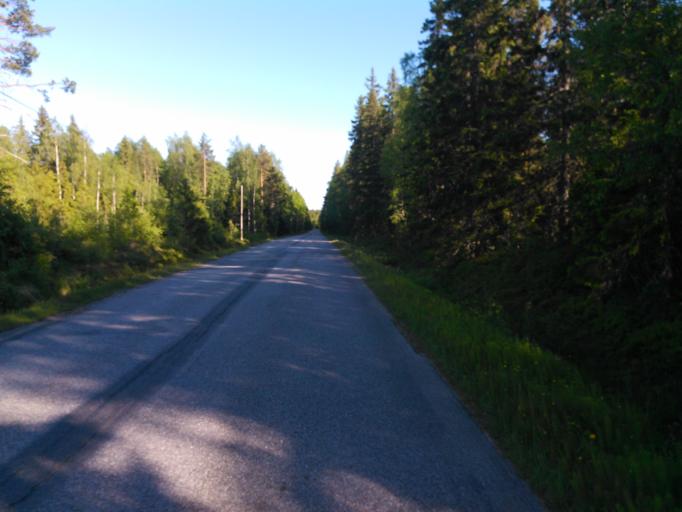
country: SE
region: Vaesterbotten
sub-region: Umea Kommun
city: Ersmark
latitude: 63.8739
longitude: 20.3277
